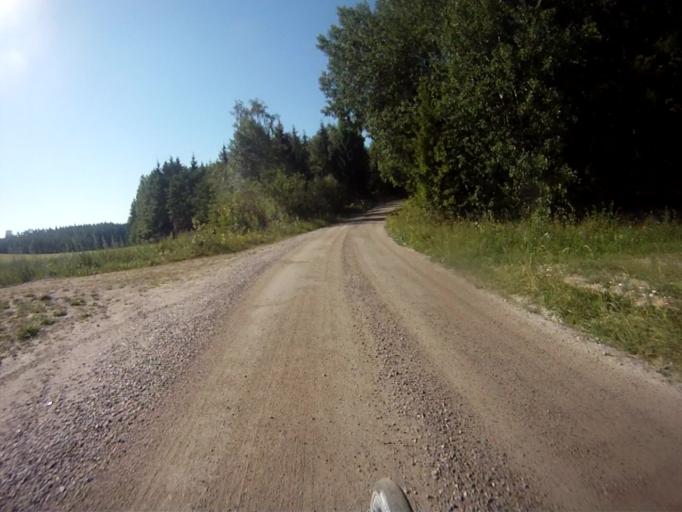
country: SE
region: Soedermanland
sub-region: Katrineholms Kommun
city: Katrineholm
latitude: 59.0651
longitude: 16.2755
